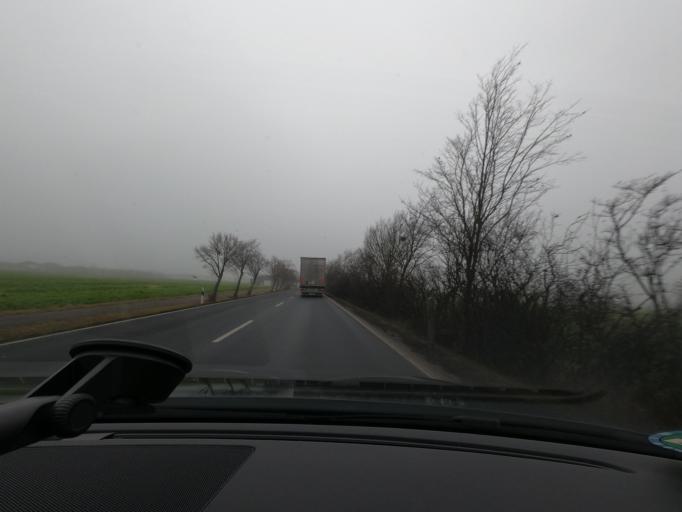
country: DE
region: North Rhine-Westphalia
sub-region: Regierungsbezirk Koln
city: Merzenich
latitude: 50.8260
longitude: 6.5400
